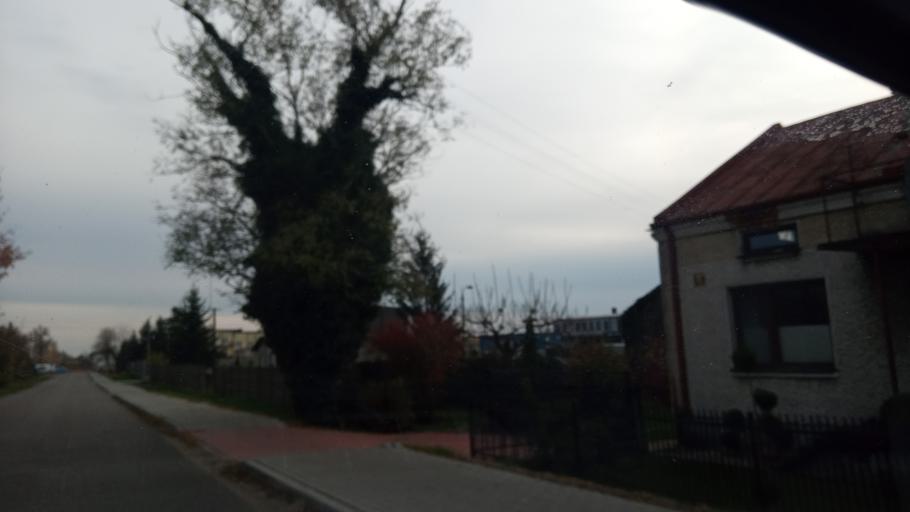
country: PL
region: Lodz Voivodeship
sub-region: Powiat skierniewicki
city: Bolimow
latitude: 52.1616
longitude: 20.1743
